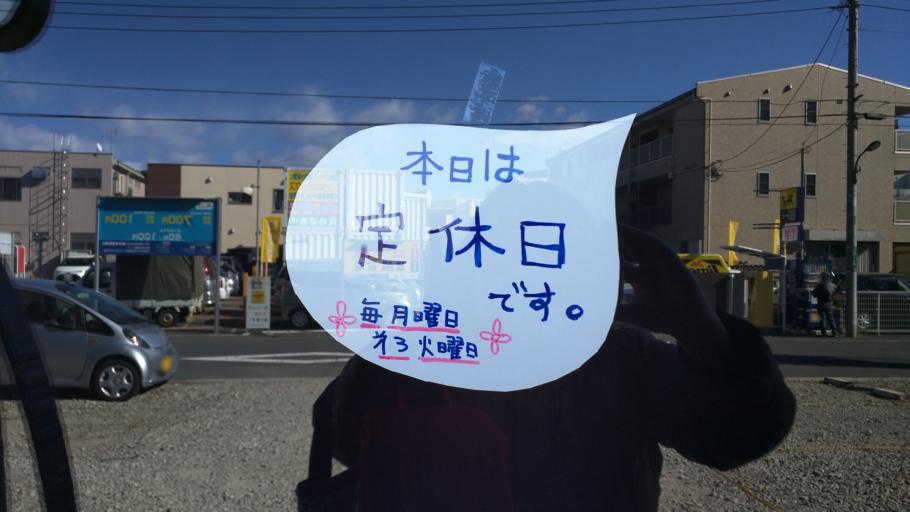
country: JP
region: Tokyo
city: Kokubunji
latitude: 35.6708
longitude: 139.4587
